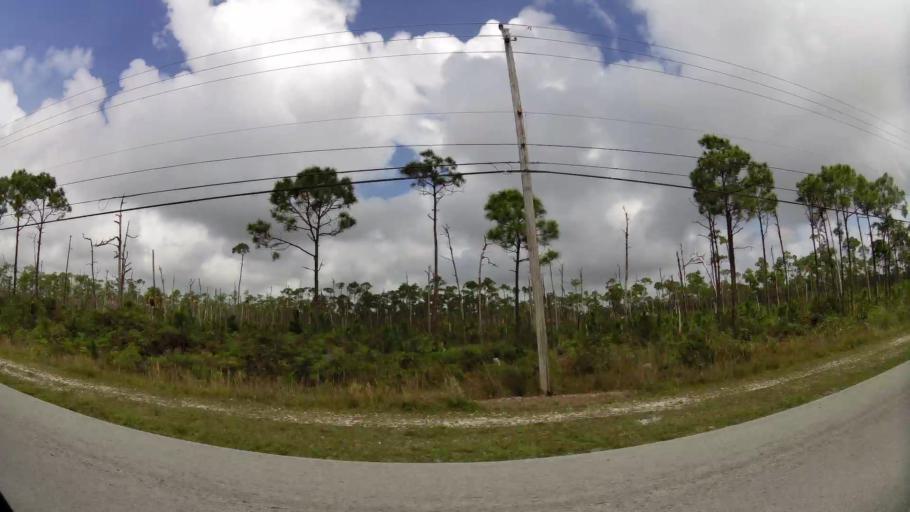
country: BS
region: Freeport
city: Lucaya
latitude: 26.5330
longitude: -78.6130
